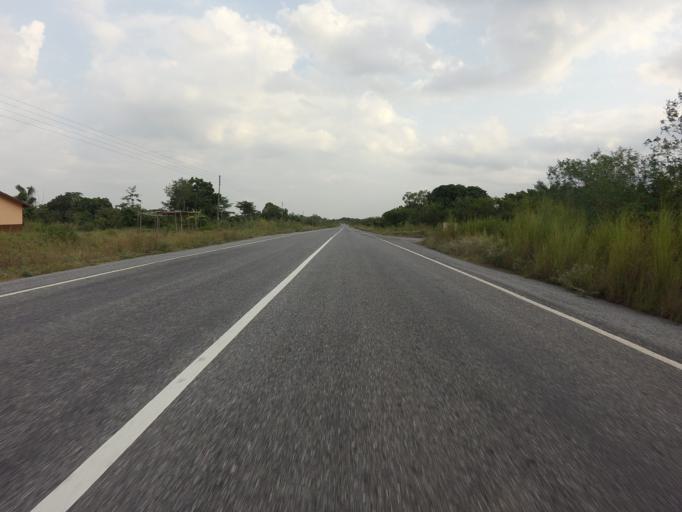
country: GH
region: Volta
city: Ho
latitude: 6.3595
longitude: 0.5364
